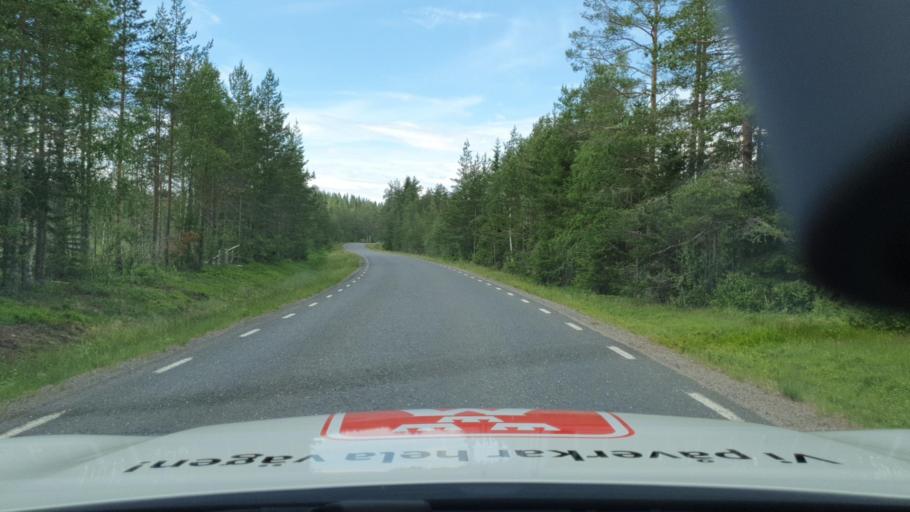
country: SE
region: Vaermland
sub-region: Torsby Kommun
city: Torsby
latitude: 60.5304
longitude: 12.8232
